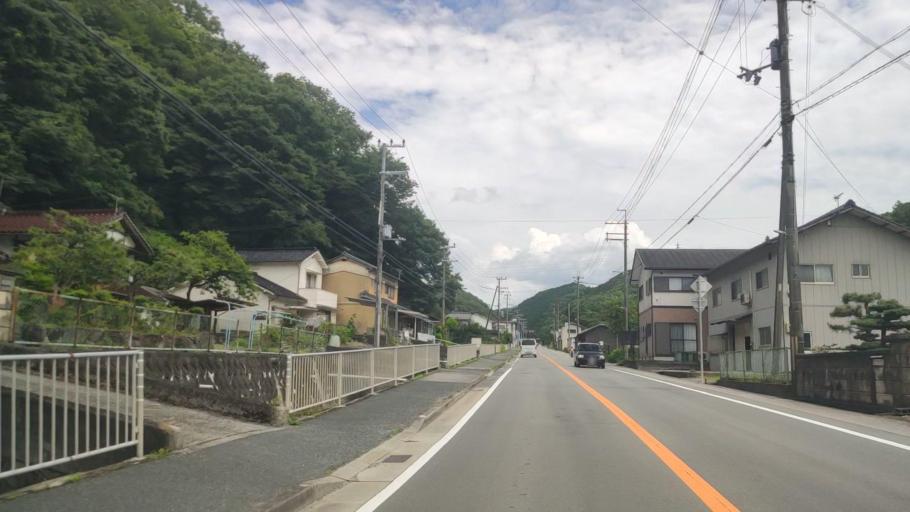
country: JP
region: Hyogo
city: Yamazakicho-nakabirose
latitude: 35.0051
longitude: 134.3647
